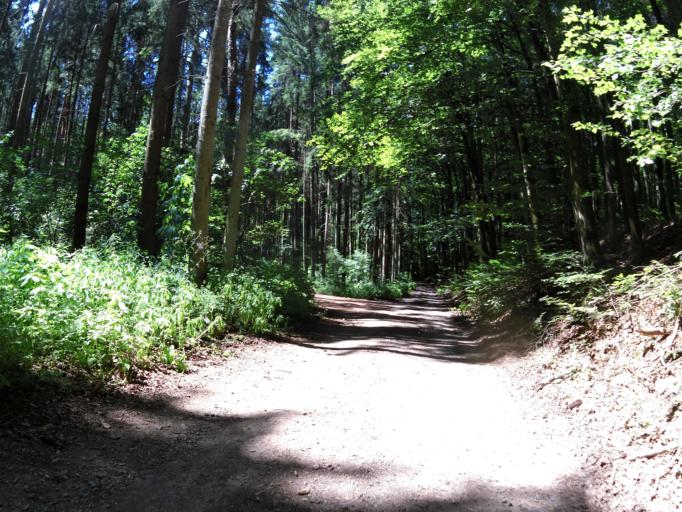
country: DE
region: Bavaria
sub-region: Regierungsbezirk Unterfranken
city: Reichenberg
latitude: 49.7208
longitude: 9.8929
